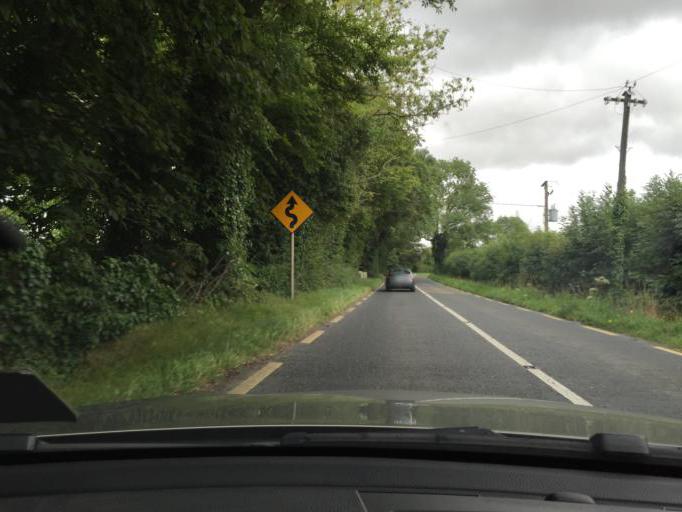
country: IE
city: Confey
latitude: 53.3974
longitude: -6.5411
